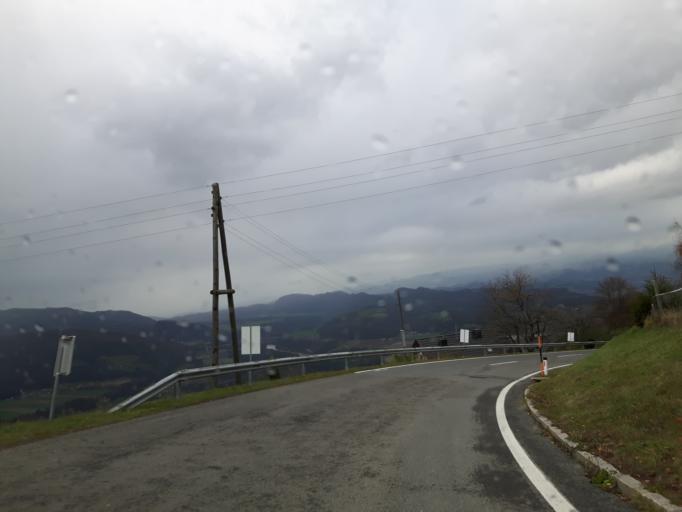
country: AT
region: Carinthia
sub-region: Politischer Bezirk Wolfsberg
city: Lavamund
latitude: 46.6436
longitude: 14.9754
